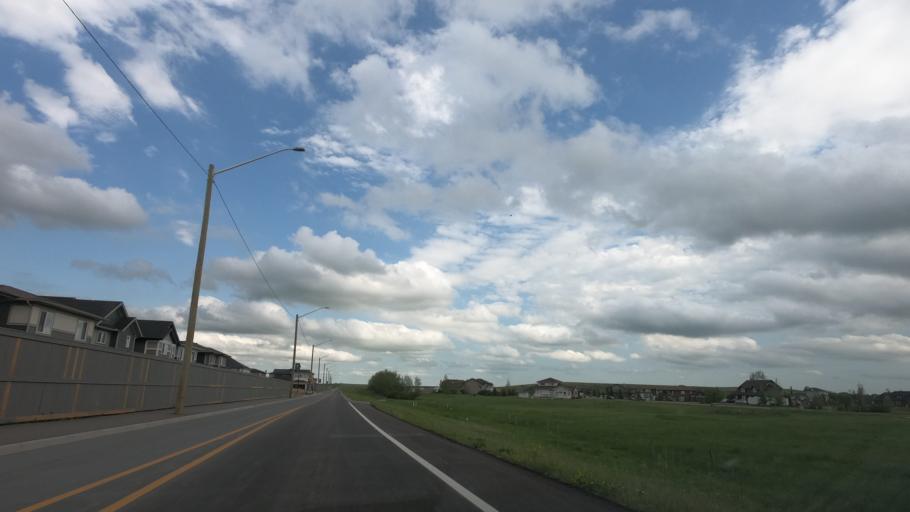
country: CA
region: Alberta
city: Airdrie
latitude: 51.2564
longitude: -113.9893
